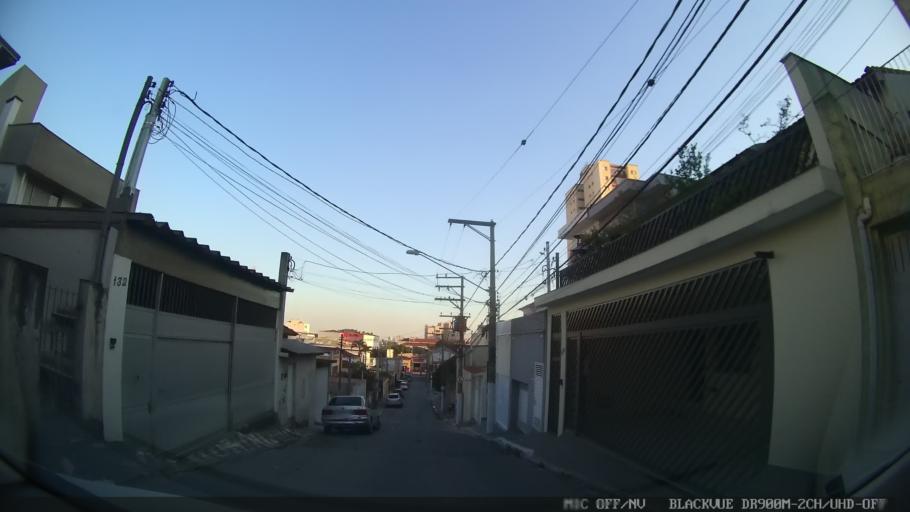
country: BR
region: Sao Paulo
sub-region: Sao Paulo
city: Sao Paulo
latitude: -23.4991
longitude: -46.6346
